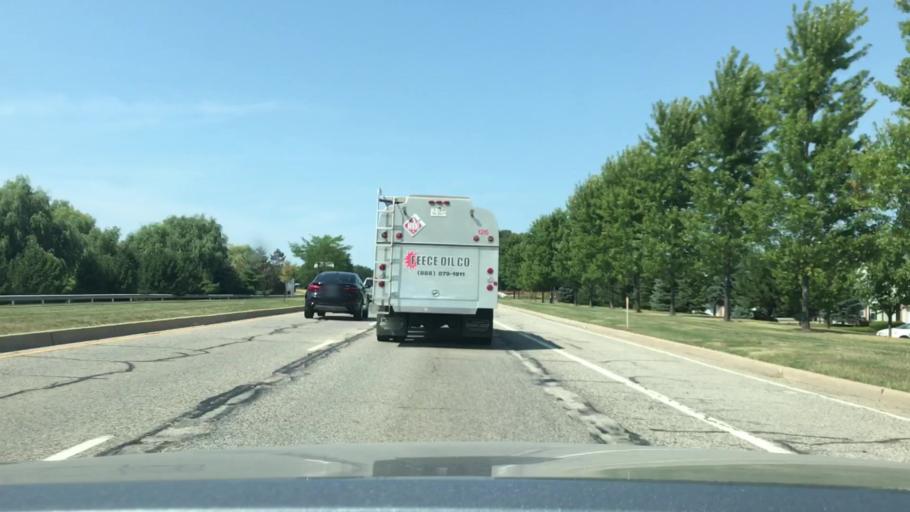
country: US
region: Illinois
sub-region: Kane County
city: Batavia
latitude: 41.8198
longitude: -88.2797
